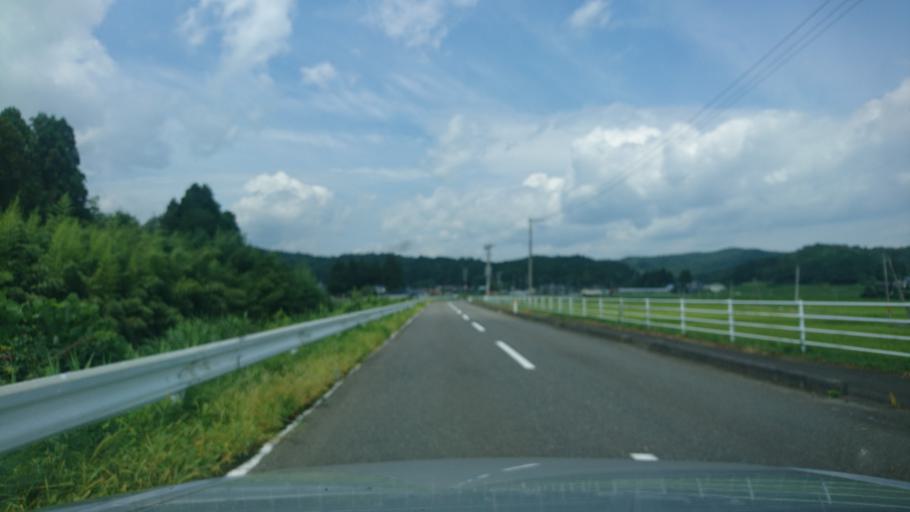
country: JP
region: Iwate
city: Ichinoseki
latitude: 38.8196
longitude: 140.9355
